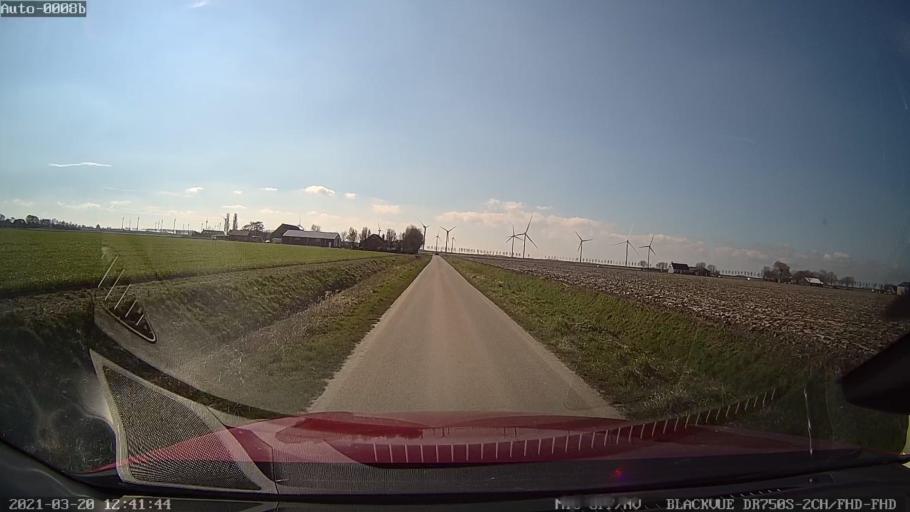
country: NL
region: South Holland
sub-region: Gemeente Goeree-Overflakkee
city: Middelharnis
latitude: 51.7044
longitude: 4.1874
